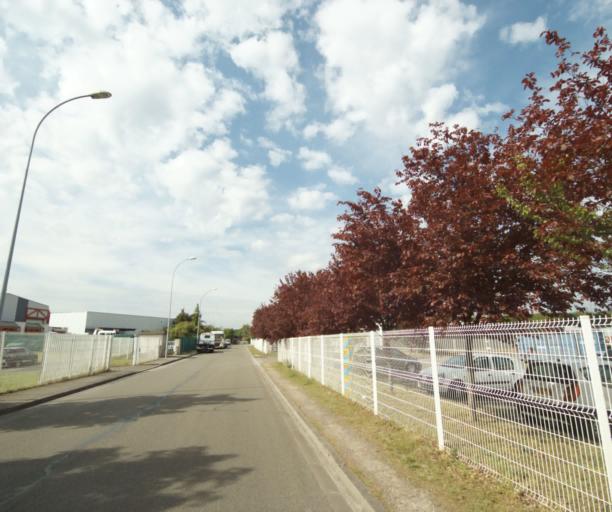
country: FR
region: Ile-de-France
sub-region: Departement des Yvelines
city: Bouafle
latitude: 48.9786
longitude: 1.8917
